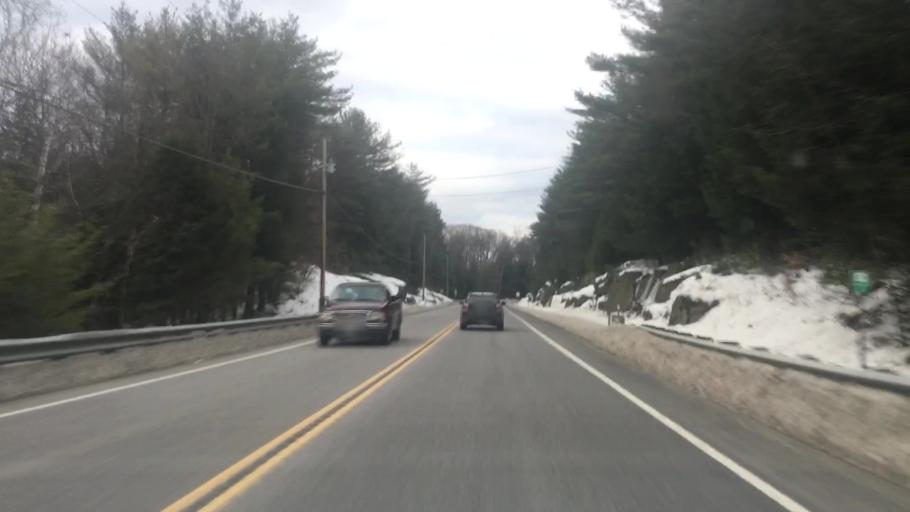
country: US
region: New Hampshire
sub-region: Hillsborough County
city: Antrim
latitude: 43.0778
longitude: -71.9908
